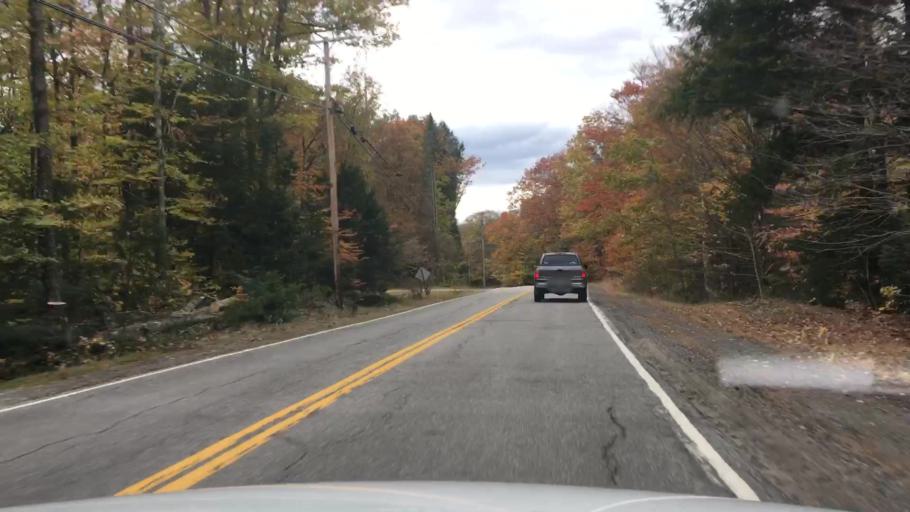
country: US
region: Maine
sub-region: Kennebec County
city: Monmouth
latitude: 44.1347
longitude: -69.9862
